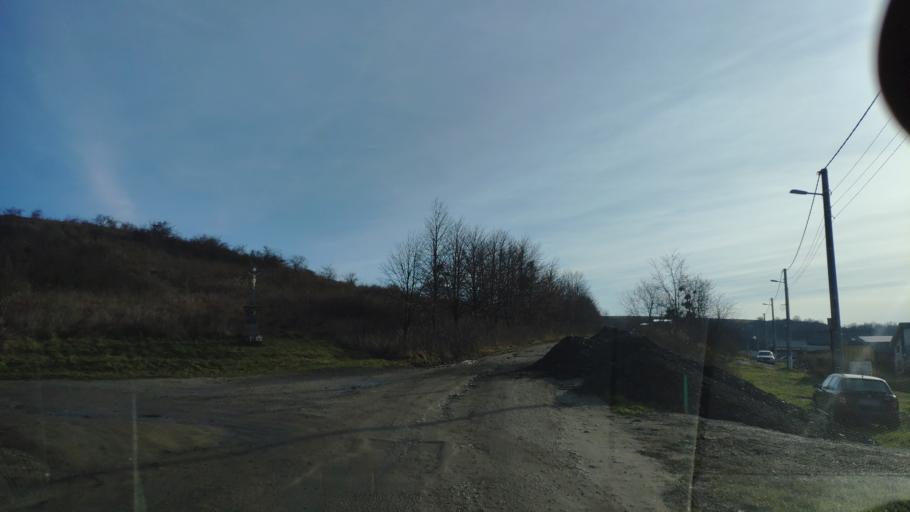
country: SK
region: Kosicky
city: Kosice
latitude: 48.6888
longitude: 21.3505
